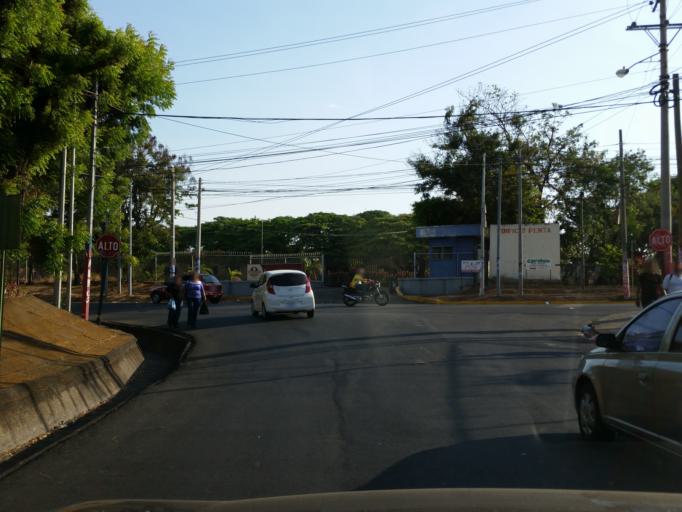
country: NI
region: Managua
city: Managua
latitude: 12.1250
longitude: -86.2662
